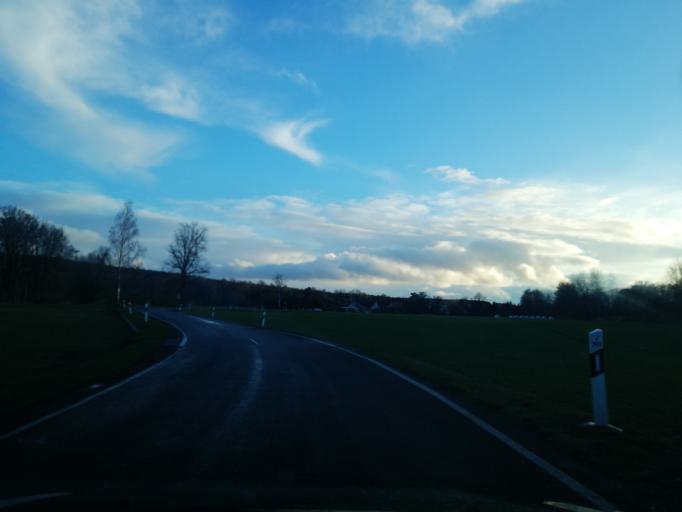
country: DE
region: Brandenburg
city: Calau
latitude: 51.7229
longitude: 13.9466
